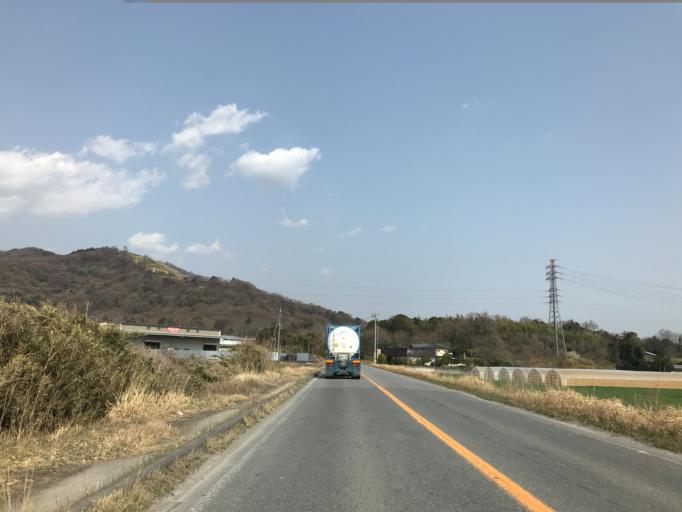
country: JP
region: Ibaraki
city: Tsukuba
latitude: 36.1468
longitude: 140.1250
